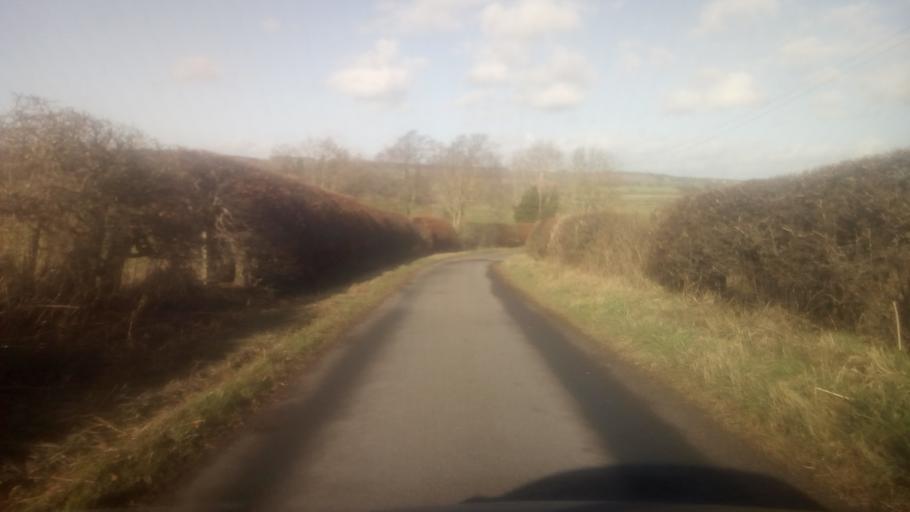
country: GB
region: Scotland
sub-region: The Scottish Borders
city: Jedburgh
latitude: 55.5082
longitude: -2.5031
